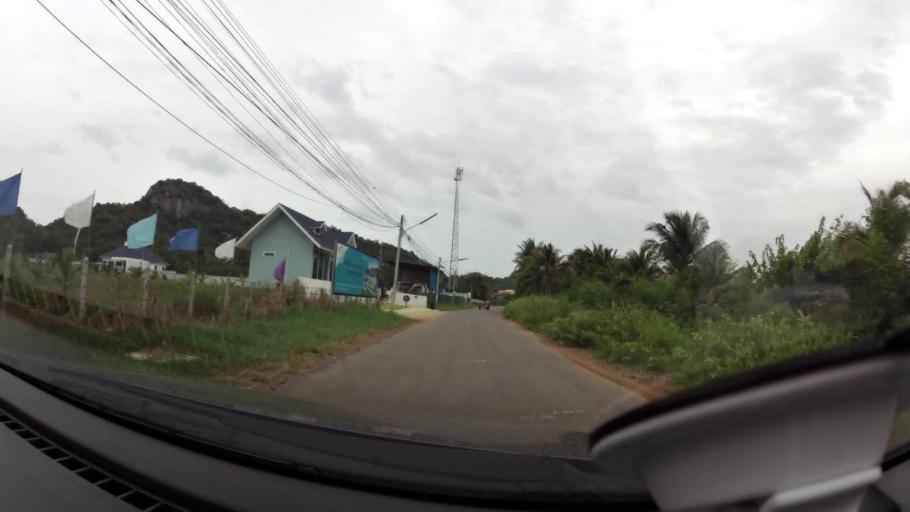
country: TH
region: Prachuap Khiri Khan
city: Pran Buri
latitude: 12.4483
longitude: 99.9712
